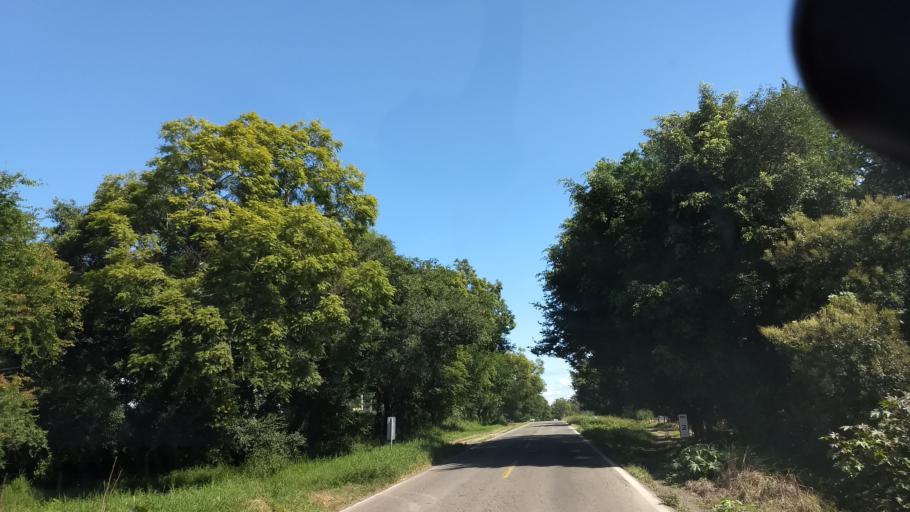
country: MX
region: Jalisco
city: Tuxpan
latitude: 19.5418
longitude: -103.4055
